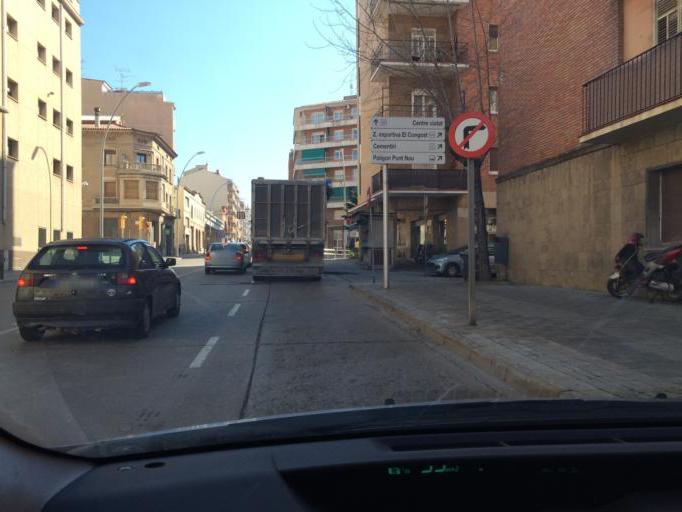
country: ES
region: Catalonia
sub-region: Provincia de Barcelona
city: Manresa
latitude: 41.7266
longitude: 1.8156
